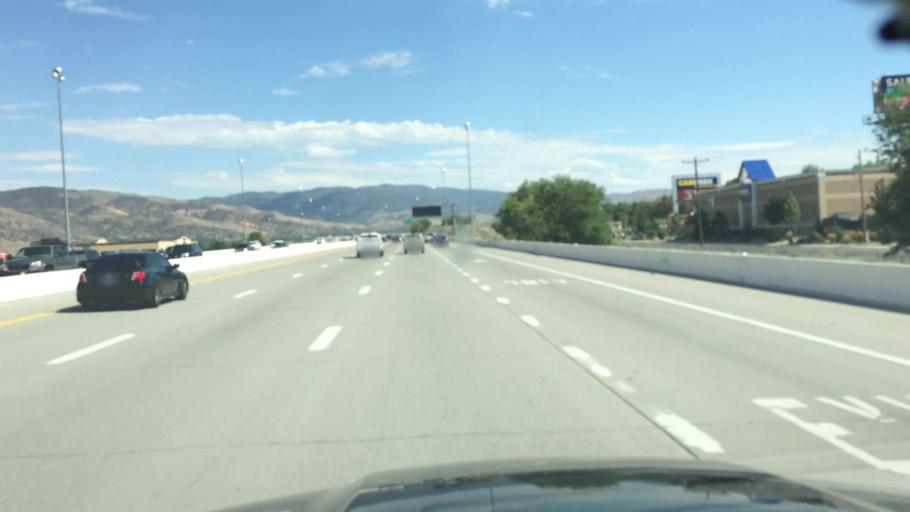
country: US
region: Nevada
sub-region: Washoe County
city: Sparks
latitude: 39.4295
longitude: -119.7583
